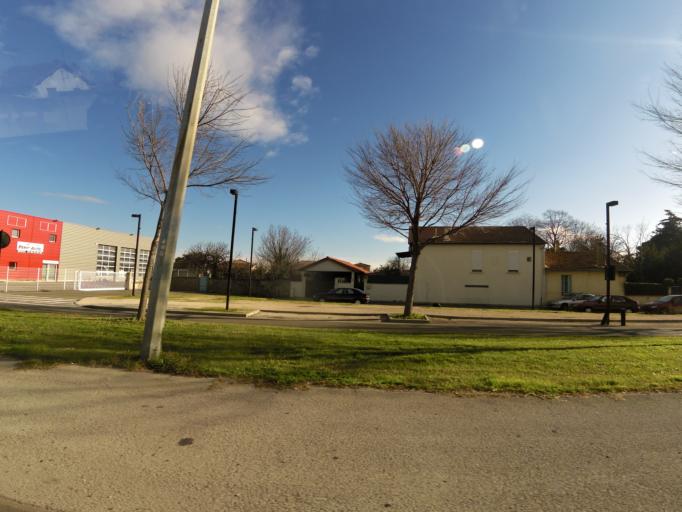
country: FR
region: Languedoc-Roussillon
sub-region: Departement du Gard
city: Nimes
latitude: 43.8290
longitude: 4.3777
